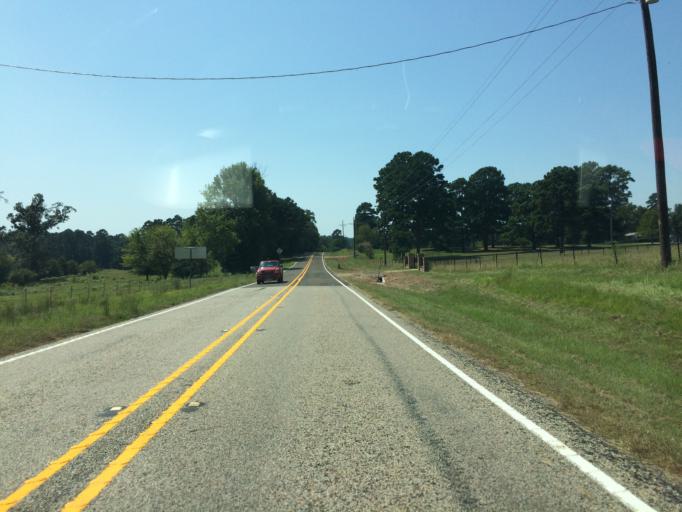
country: US
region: Texas
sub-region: Wood County
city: Quitman
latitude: 32.7411
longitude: -95.2912
